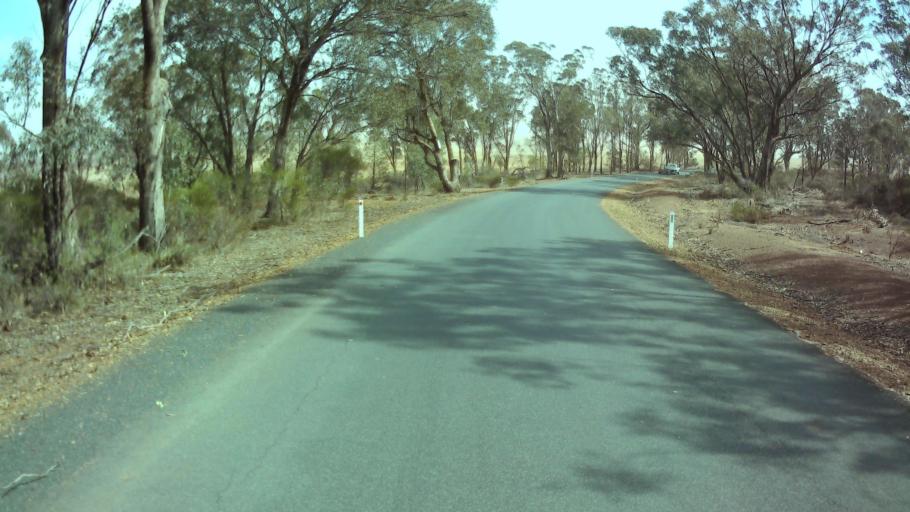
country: AU
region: New South Wales
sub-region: Weddin
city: Grenfell
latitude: -33.7752
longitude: 147.9869
